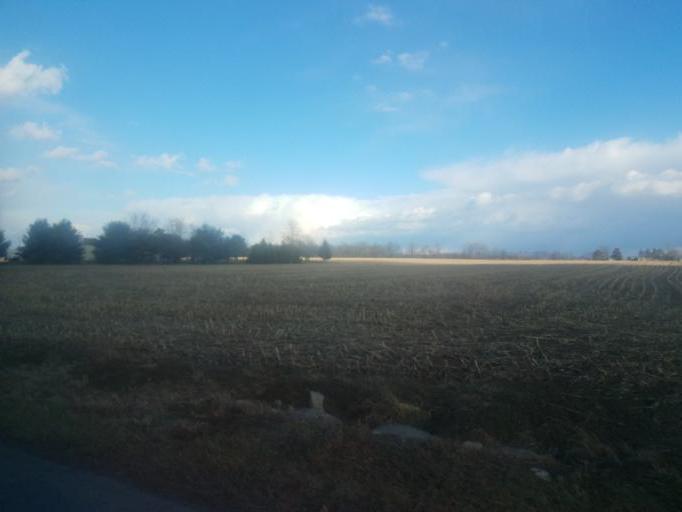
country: US
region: Ohio
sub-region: Marion County
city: Prospect
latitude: 40.4054
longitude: -83.1443
